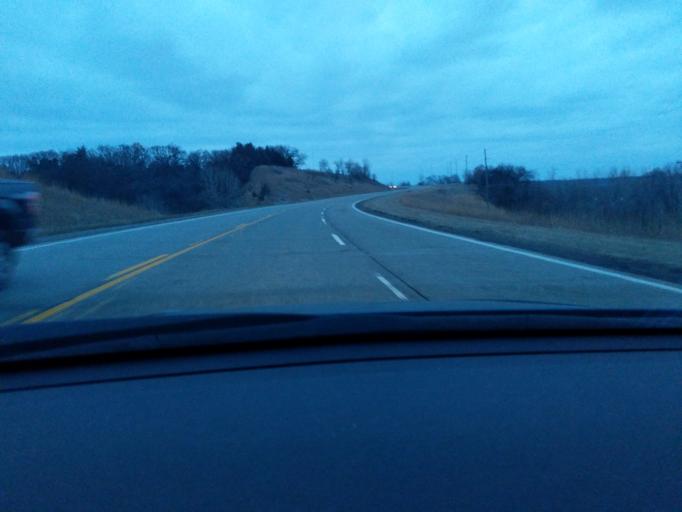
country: US
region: Minnesota
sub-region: Yellow Medicine County
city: Granite Falls
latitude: 44.8012
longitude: -95.5117
